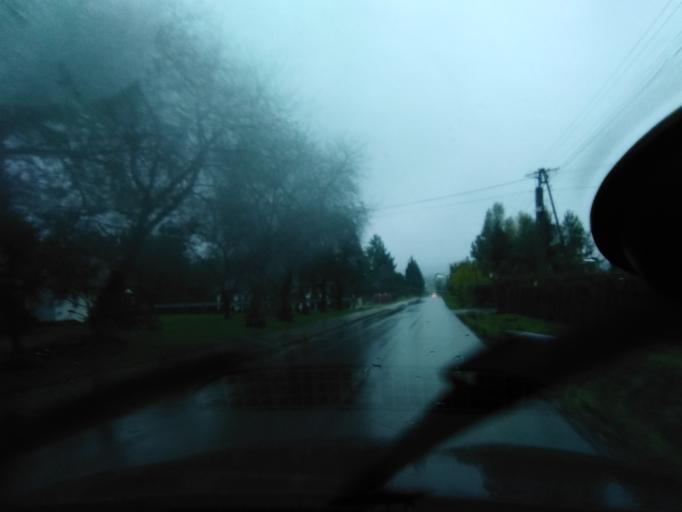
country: PL
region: Subcarpathian Voivodeship
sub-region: Powiat krosnienski
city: Kroscienko Wyzne
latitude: 49.6882
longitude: 21.8099
